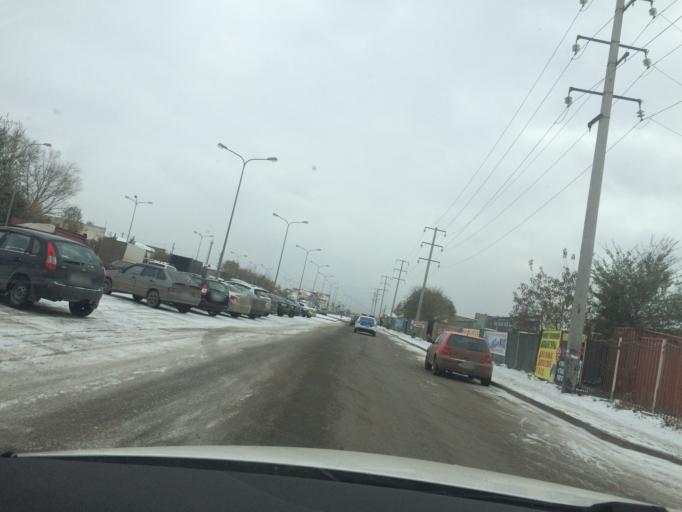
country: KZ
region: Astana Qalasy
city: Astana
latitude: 51.1797
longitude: 71.4655
